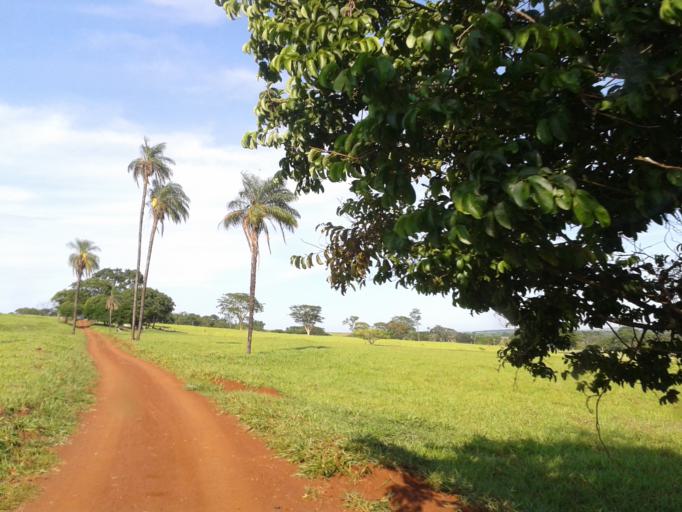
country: BR
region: Minas Gerais
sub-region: Centralina
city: Centralina
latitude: -18.7091
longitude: -49.1896
